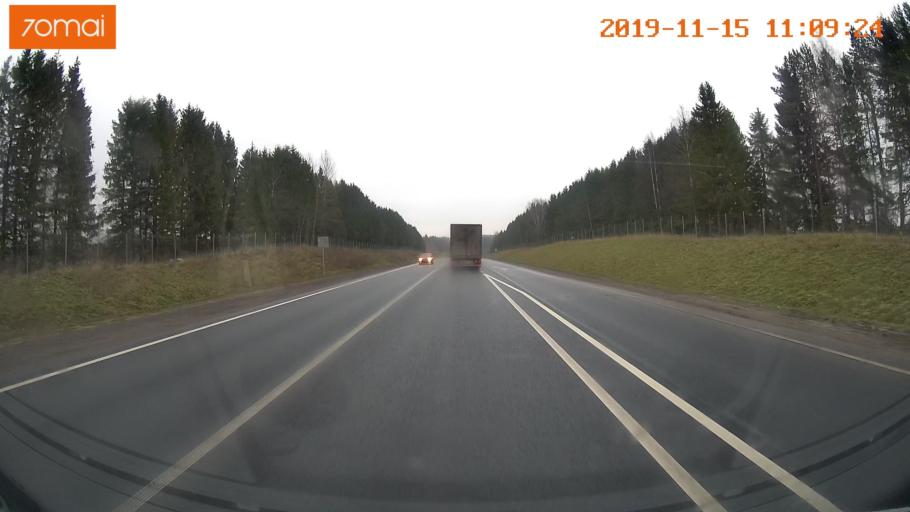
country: RU
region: Vologda
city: Chebsara
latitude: 59.1204
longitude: 39.0966
